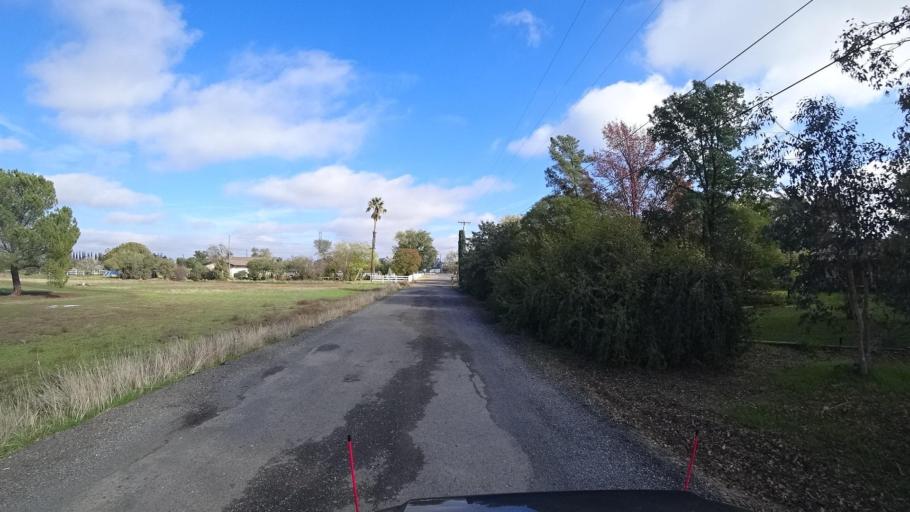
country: US
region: California
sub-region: Sacramento County
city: Vineyard
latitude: 38.4490
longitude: -121.3379
